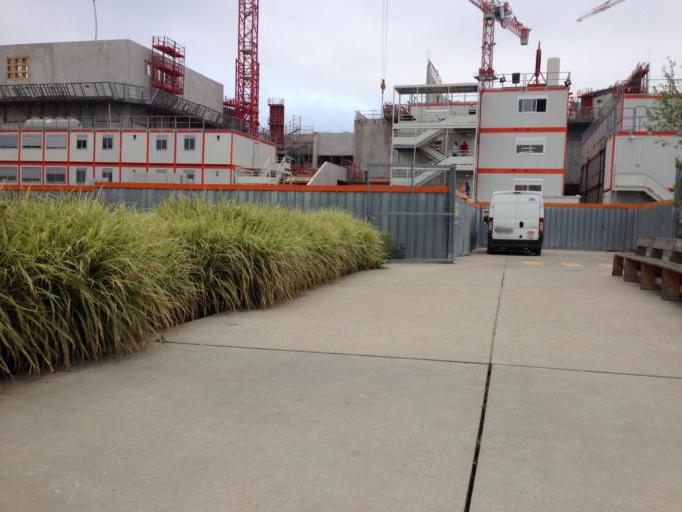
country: FR
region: Ile-de-France
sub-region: Departement des Hauts-de-Seine
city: Meudon
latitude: 48.8247
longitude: 2.2318
